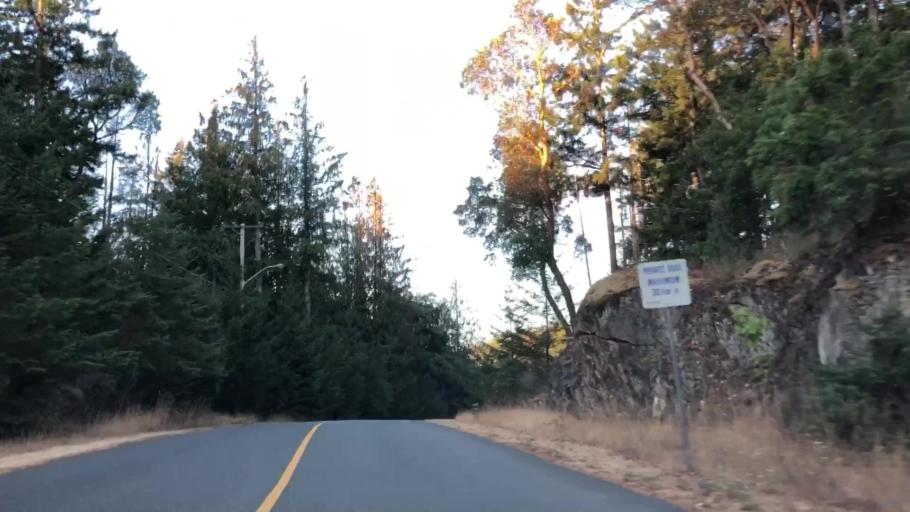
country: CA
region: British Columbia
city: Metchosin
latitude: 48.4088
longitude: -123.5129
